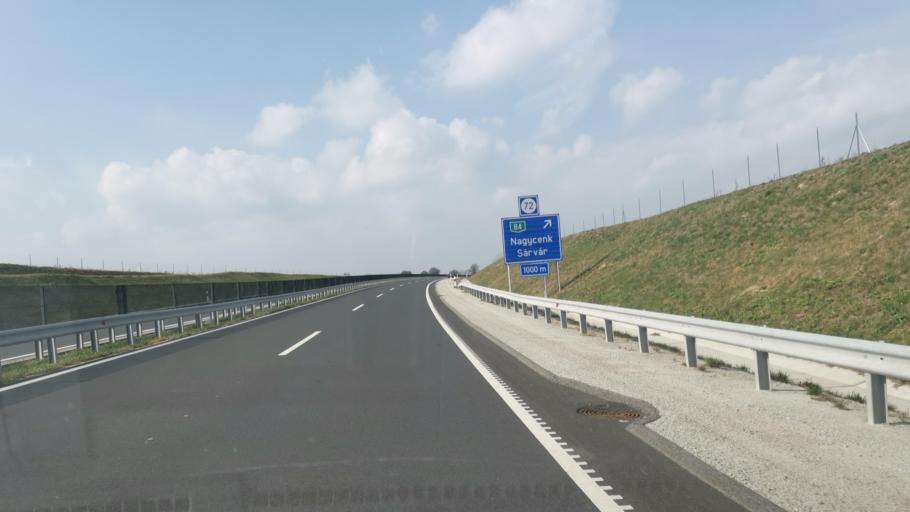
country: HU
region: Gyor-Moson-Sopron
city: Nagycenk
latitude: 47.5824
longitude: 16.7247
